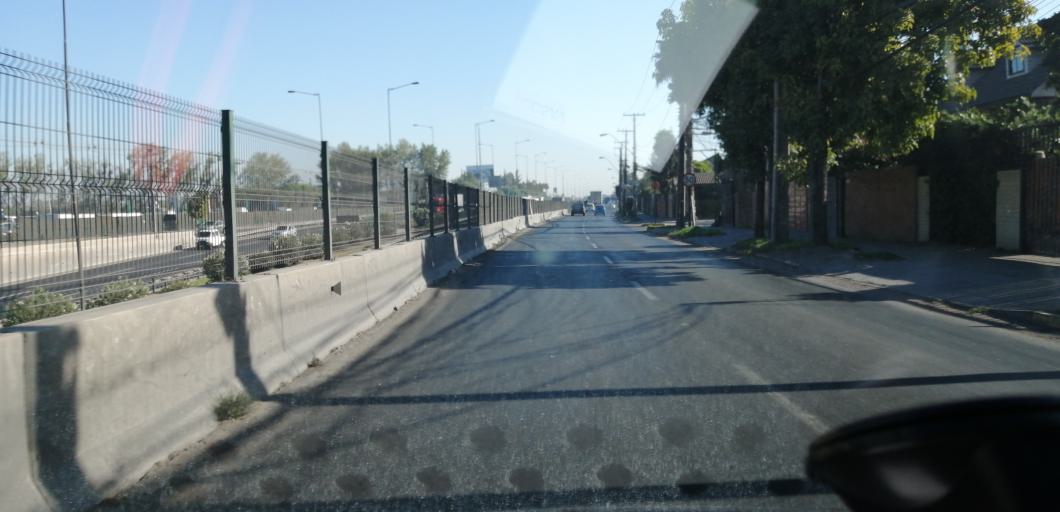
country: CL
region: Santiago Metropolitan
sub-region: Provincia de Santiago
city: Lo Prado
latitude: -33.4692
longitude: -70.7612
